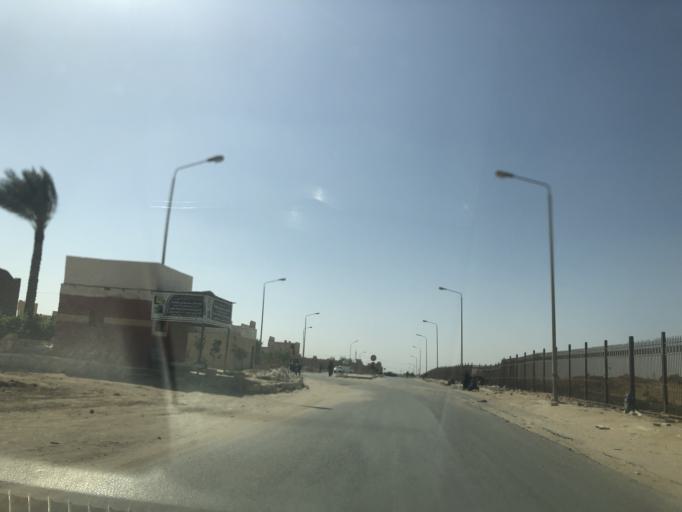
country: EG
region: Al Jizah
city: Madinat Sittah Uktubar
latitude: 29.9270
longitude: 30.9506
